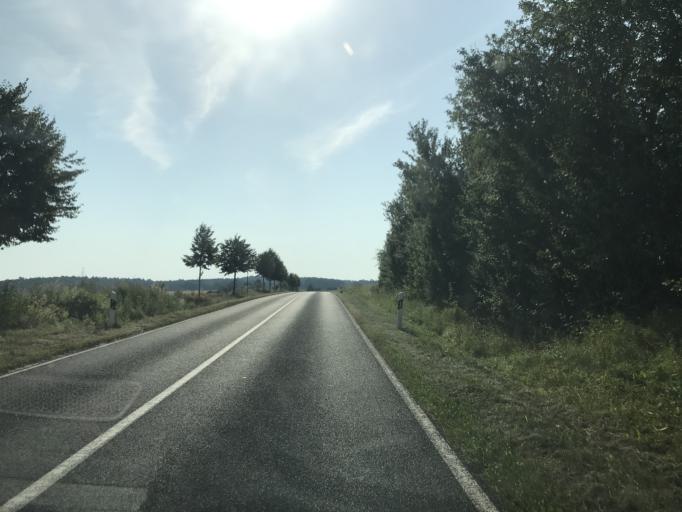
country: DE
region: Saxony-Anhalt
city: Beendorf
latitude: 52.2430
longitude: 11.1453
